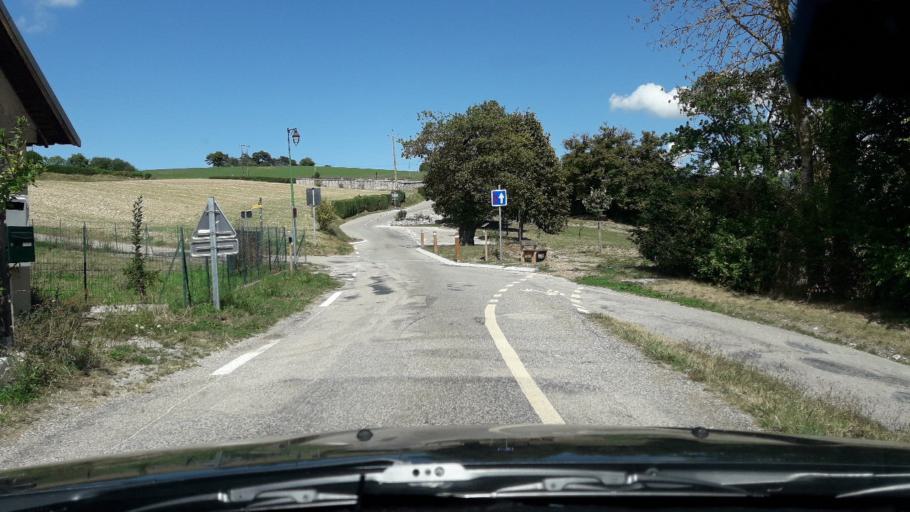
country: FR
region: Rhone-Alpes
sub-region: Departement de l'Isere
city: Mens
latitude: 44.8463
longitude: 5.6231
